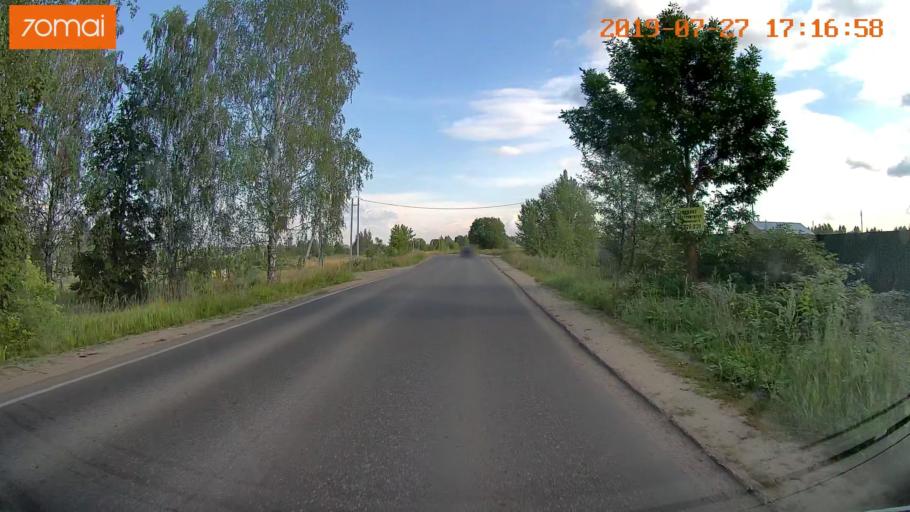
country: RU
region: Ivanovo
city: Novo-Talitsy
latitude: 57.0420
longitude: 40.8909
